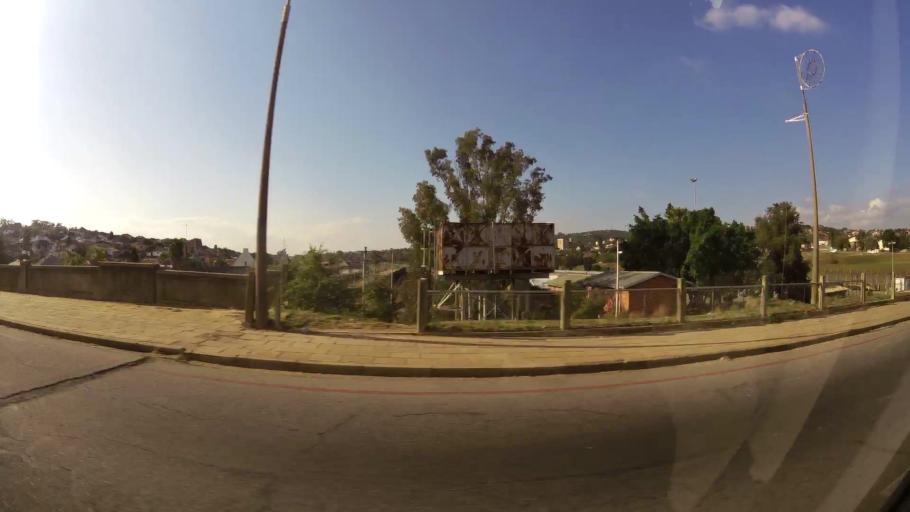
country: ZA
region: Eastern Cape
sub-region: Nelson Mandela Bay Metropolitan Municipality
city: Uitenhage
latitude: -33.7730
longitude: 25.4078
